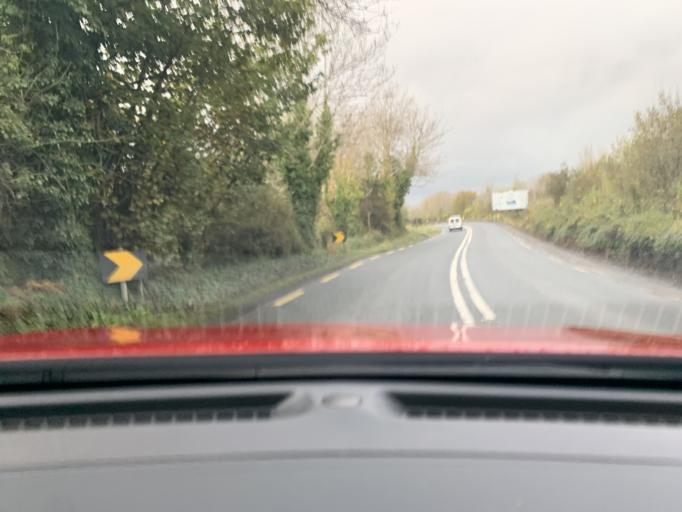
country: IE
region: Connaught
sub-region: Sligo
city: Collooney
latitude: 54.1953
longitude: -8.4952
